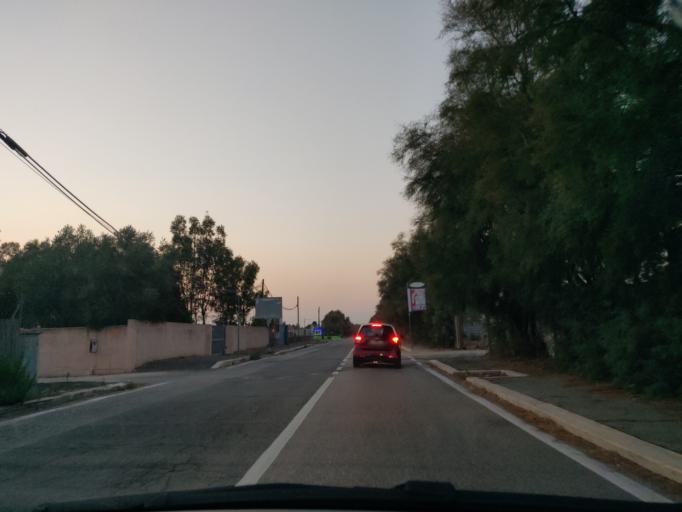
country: IT
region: Latium
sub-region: Citta metropolitana di Roma Capitale
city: Npp 23 (Parco Leonardo)
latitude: 41.8202
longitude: 12.2947
